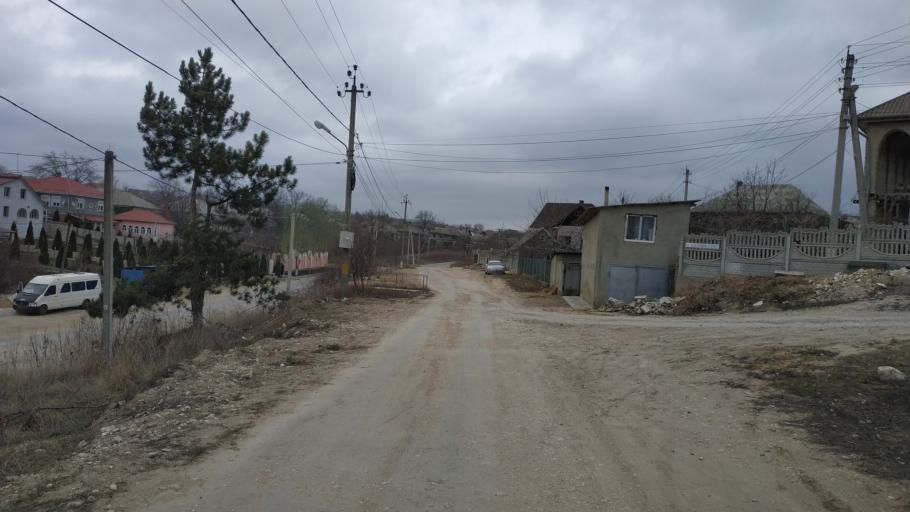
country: MD
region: Laloveni
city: Ialoveni
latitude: 46.9350
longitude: 28.7938
